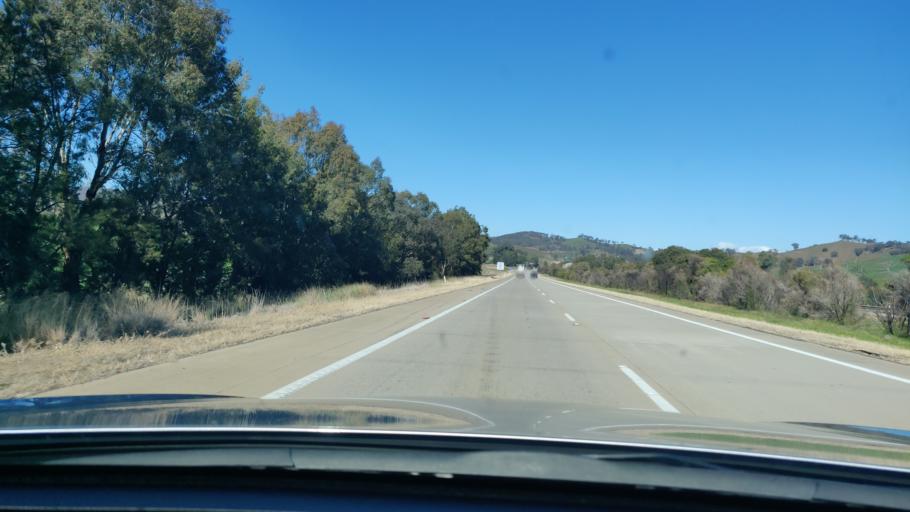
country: AU
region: New South Wales
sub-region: Gundagai
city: Gundagai
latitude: -35.1899
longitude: 147.8187
